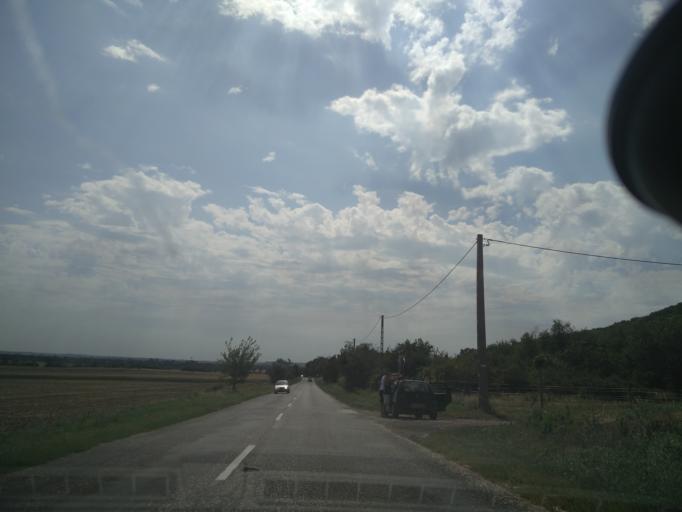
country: HU
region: Fejer
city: Velence
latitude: 47.2542
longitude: 18.6259
